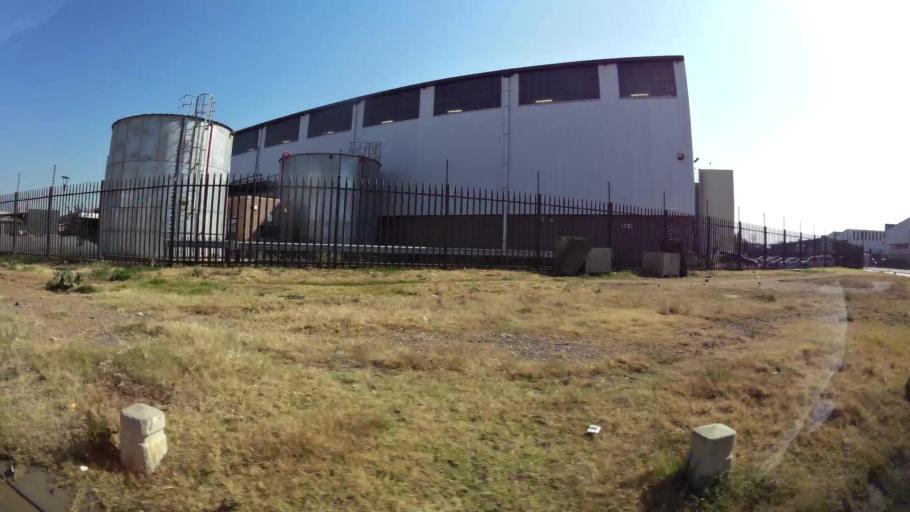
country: ZA
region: Gauteng
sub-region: Ekurhuleni Metropolitan Municipality
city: Boksburg
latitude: -26.1729
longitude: 28.2285
